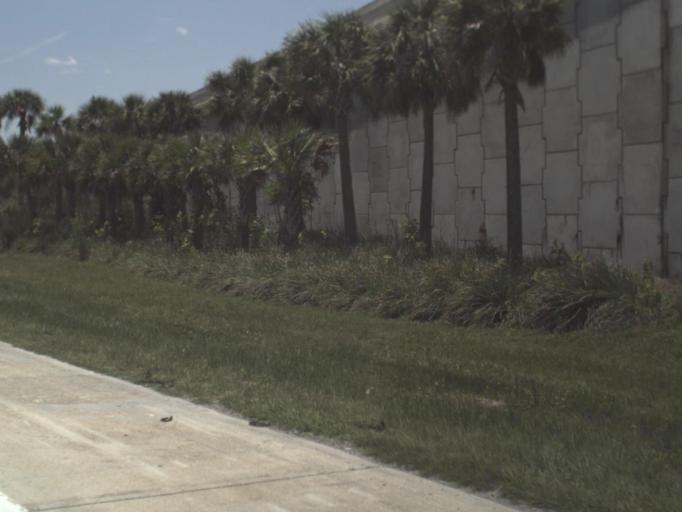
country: US
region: Florida
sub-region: Saint Johns County
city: Fruit Cove
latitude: 30.1983
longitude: -81.5569
